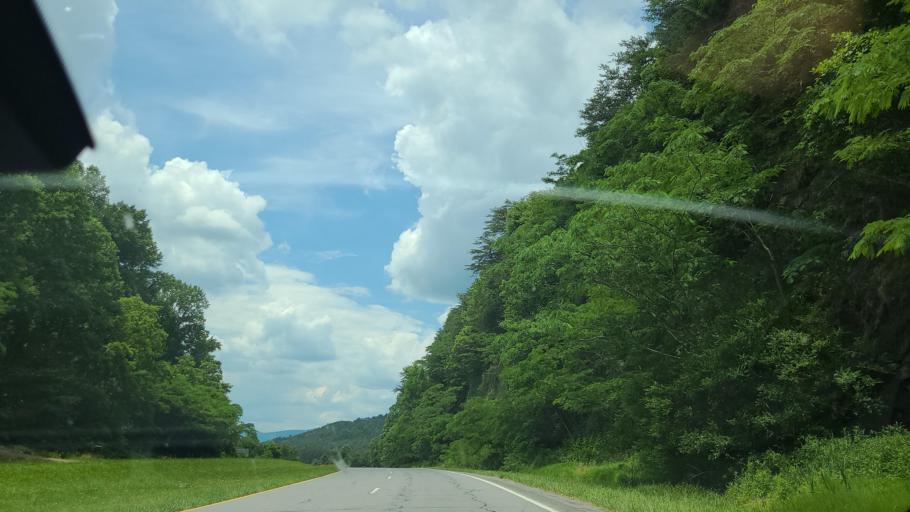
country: US
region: Georgia
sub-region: Fannin County
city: McCaysville
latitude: 35.0203
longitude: -84.3151
